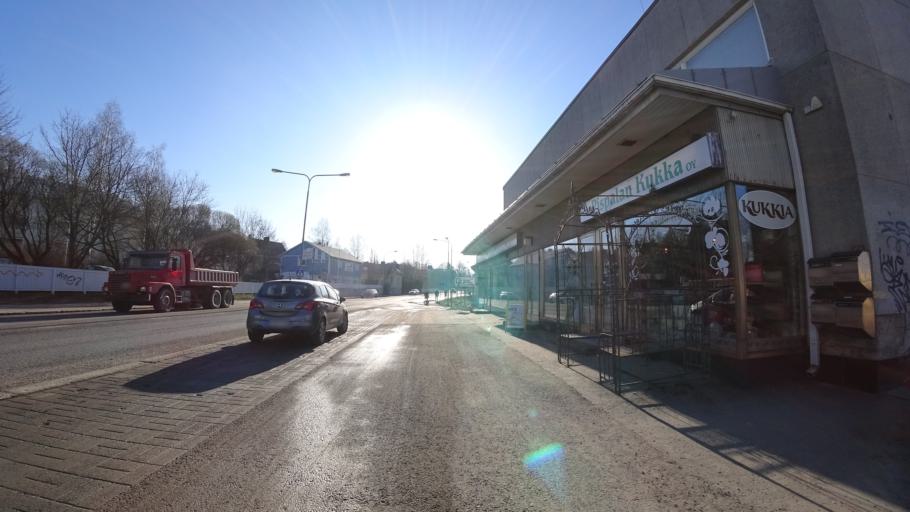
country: FI
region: Pirkanmaa
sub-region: Tampere
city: Pirkkala
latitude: 61.5072
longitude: 23.6921
